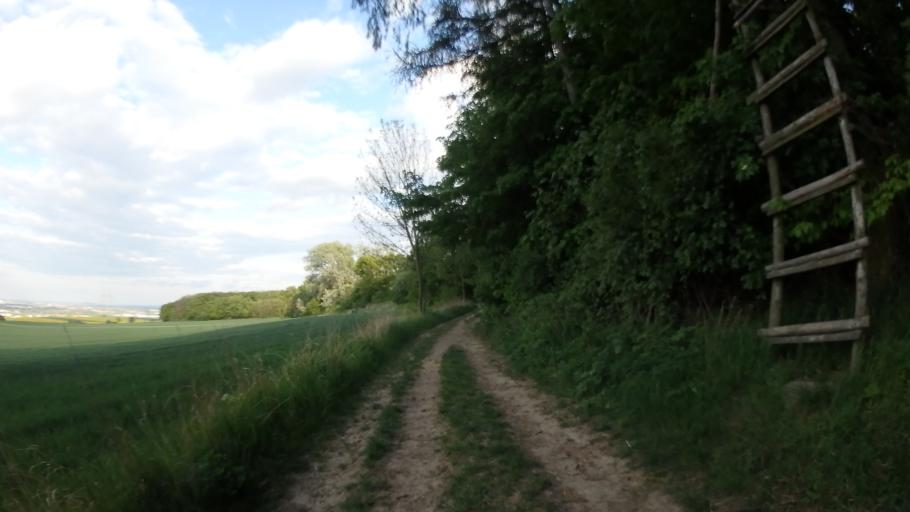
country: CZ
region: South Moravian
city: Moravany
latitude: 49.1355
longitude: 16.5691
